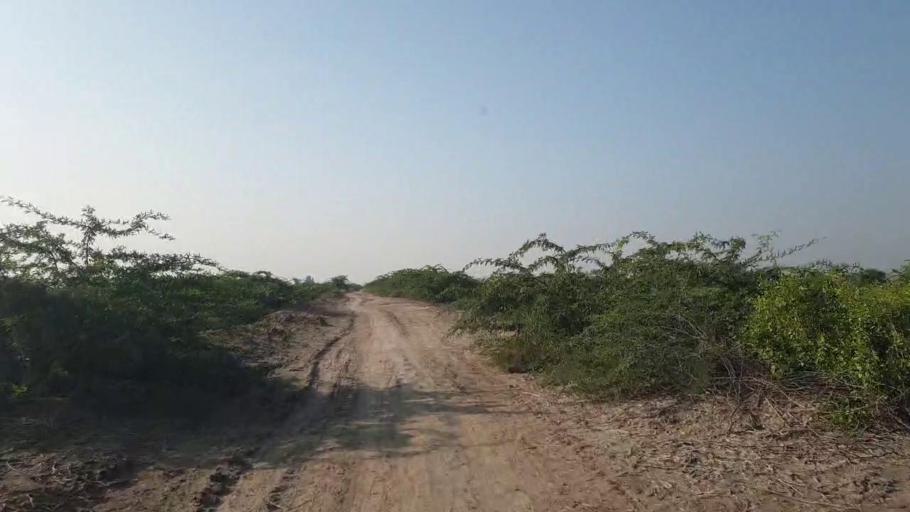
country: PK
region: Sindh
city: Badin
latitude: 24.4751
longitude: 68.7421
